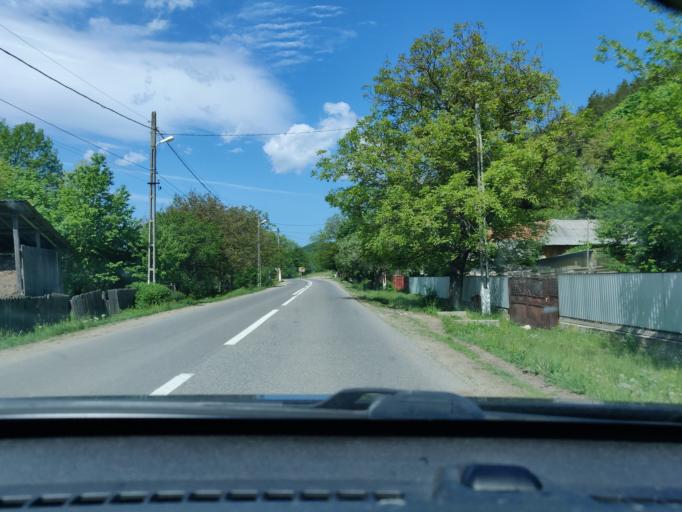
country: RO
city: Campurile de Jos
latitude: 46.0374
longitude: 26.7431
